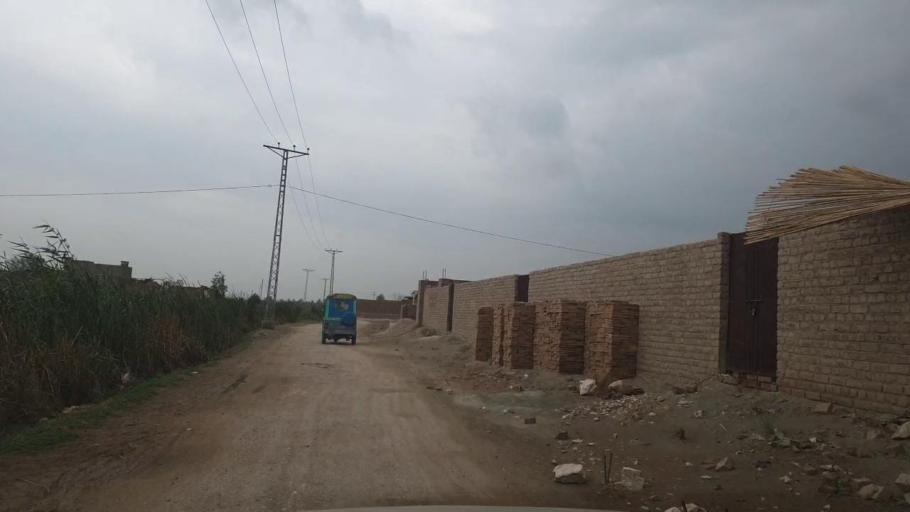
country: PK
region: Sindh
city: Khairpur
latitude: 27.5320
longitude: 68.7323
